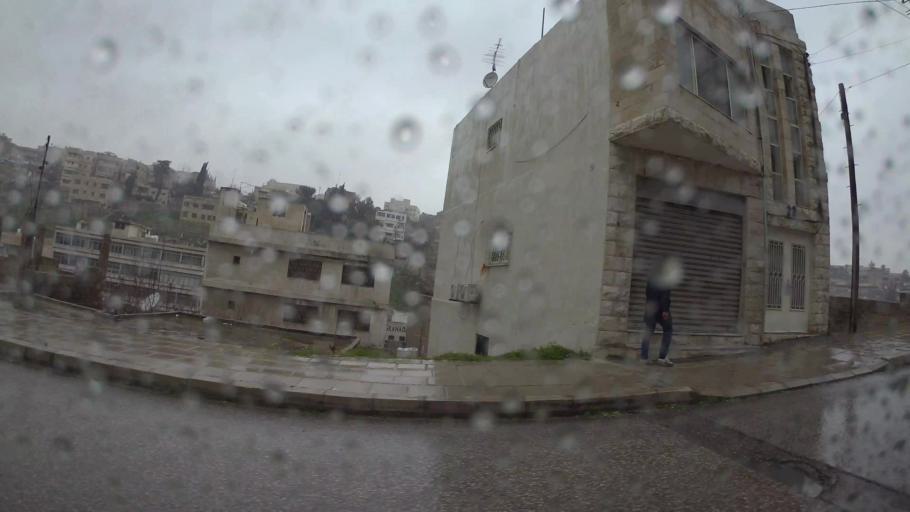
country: JO
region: Amman
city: Amman
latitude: 31.9581
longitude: 35.9274
